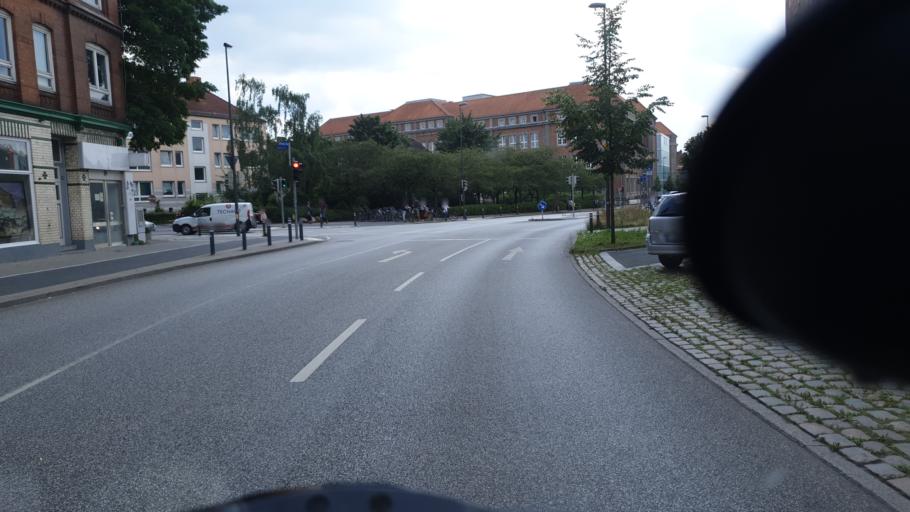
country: DE
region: Schleswig-Holstein
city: Kiel
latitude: 54.3292
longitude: 10.1286
